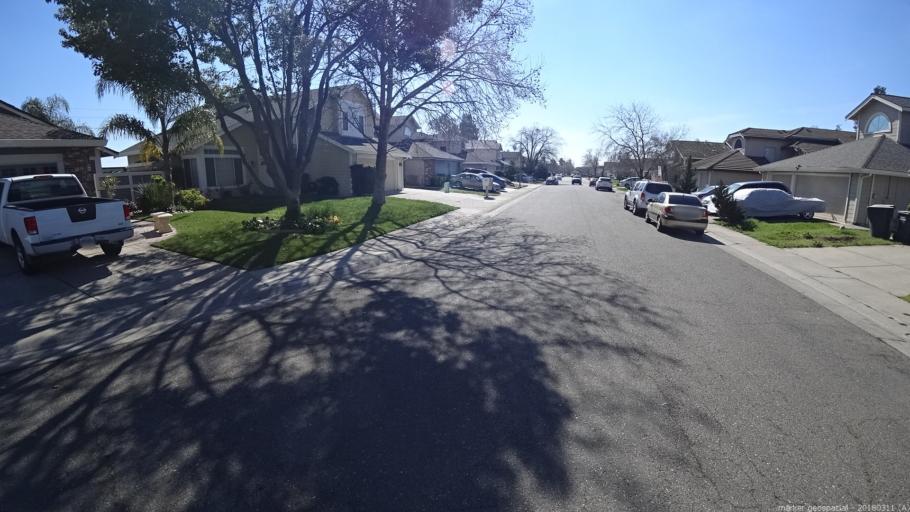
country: US
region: California
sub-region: Sacramento County
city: Florin
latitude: 38.4681
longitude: -121.3877
